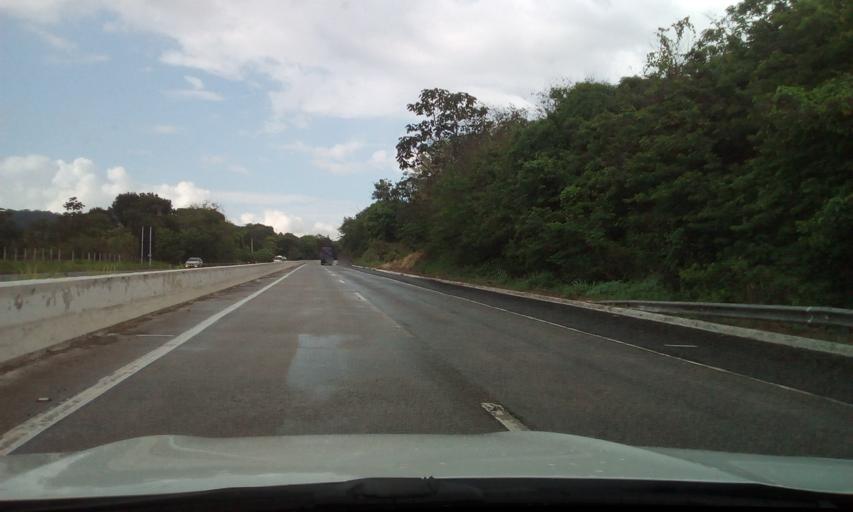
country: BR
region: Pernambuco
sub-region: Cabo De Santo Agostinho
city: Cabo
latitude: -8.3155
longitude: -35.1045
